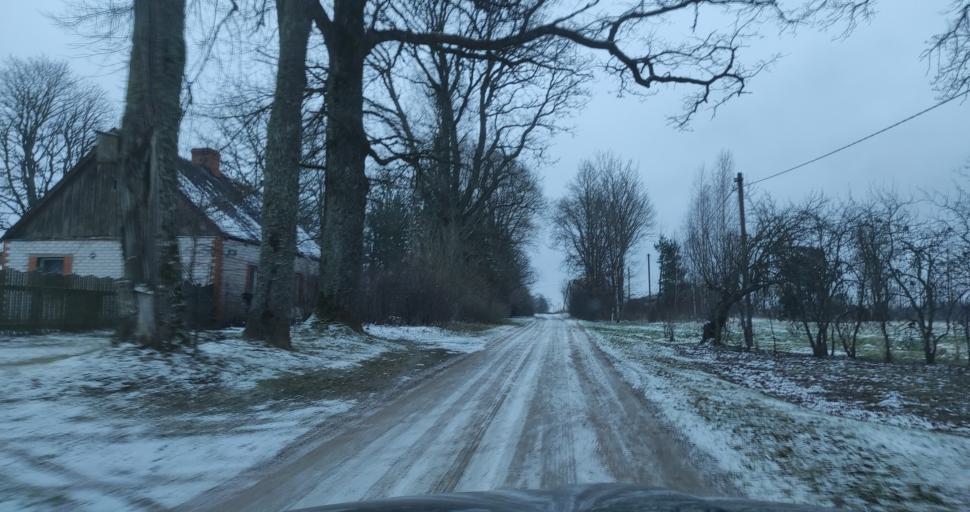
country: LV
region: Kuldigas Rajons
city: Kuldiga
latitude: 56.9733
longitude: 22.0576
